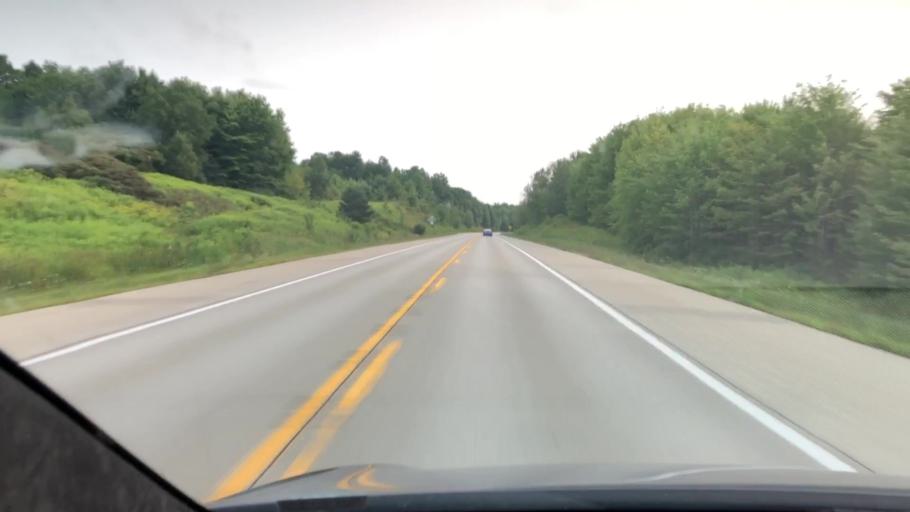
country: US
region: Pennsylvania
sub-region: Mercer County
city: Grove City
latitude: 41.2269
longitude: -79.9587
